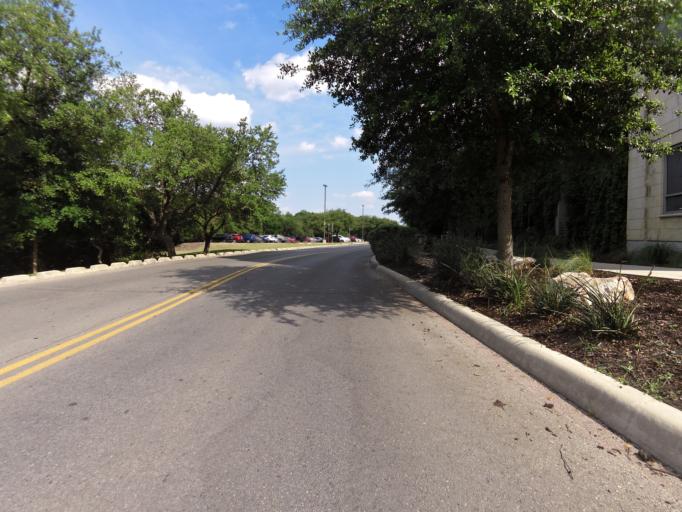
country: US
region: Texas
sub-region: Bexar County
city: Shavano Park
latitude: 29.5866
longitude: -98.6169
